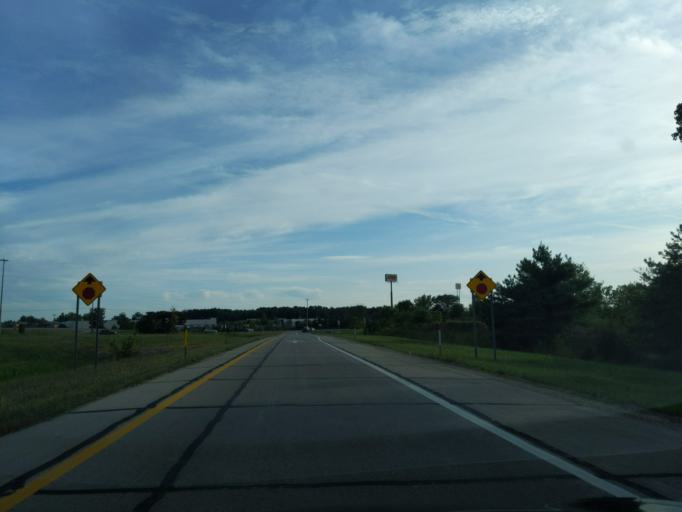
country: US
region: Michigan
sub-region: Eaton County
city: Waverly
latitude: 42.7428
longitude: -84.6697
